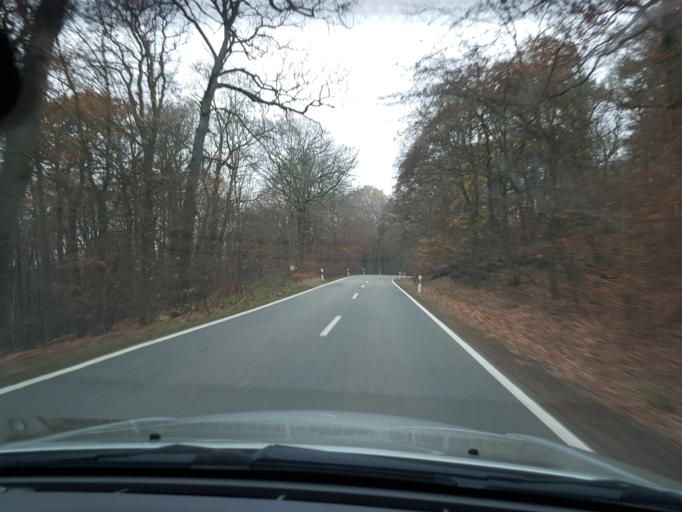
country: DE
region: Hesse
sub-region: Regierungsbezirk Darmstadt
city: Schlangenbad
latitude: 50.0895
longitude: 8.0568
